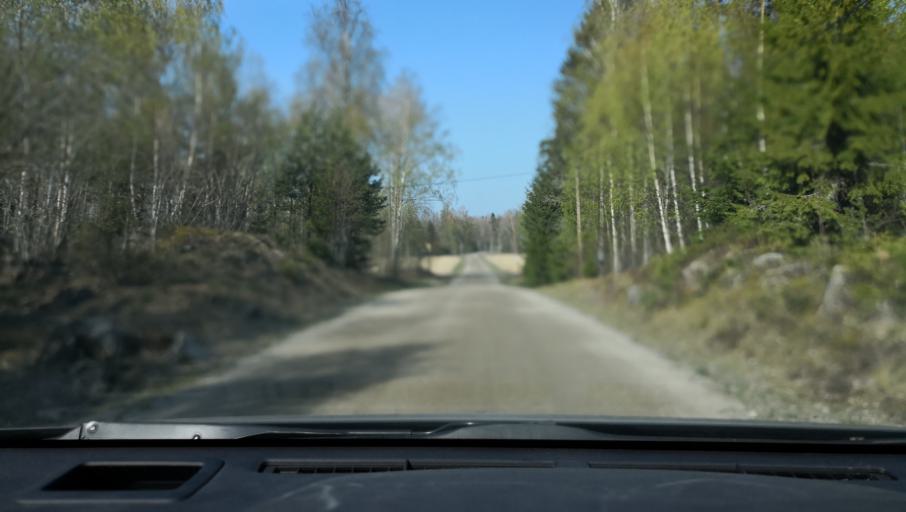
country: SE
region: Uppsala
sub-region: Heby Kommun
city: Heby
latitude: 60.0312
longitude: 16.7818
